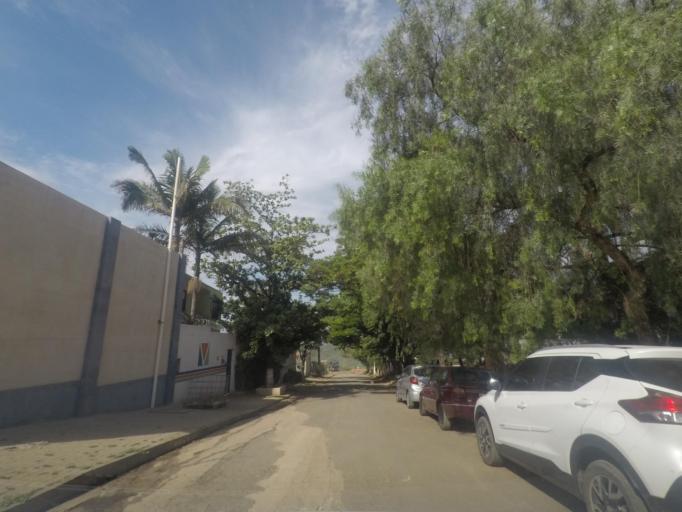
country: BR
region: Sao Paulo
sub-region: Sumare
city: Sumare
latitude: -22.7910
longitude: -47.2306
